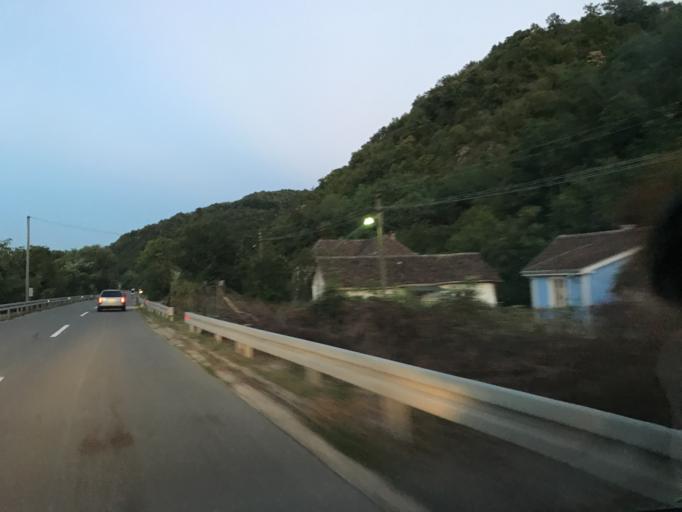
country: RO
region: Caras-Severin
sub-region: Comuna Berzasca
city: Liubcova
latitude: 44.6404
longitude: 21.9027
